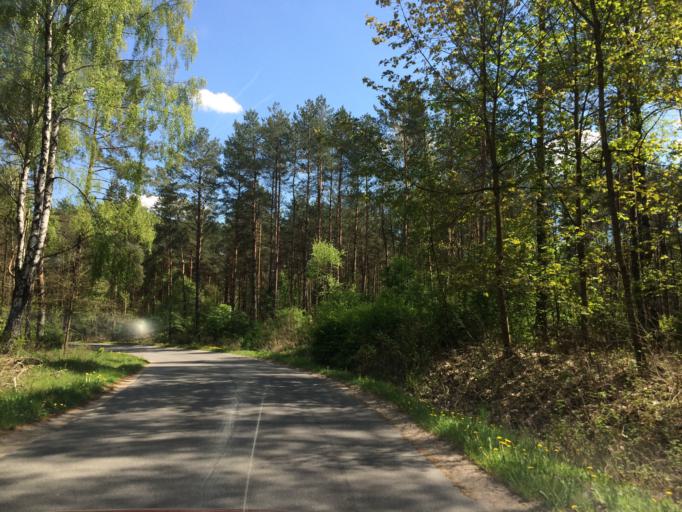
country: PL
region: Warmian-Masurian Voivodeship
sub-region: Powiat ilawski
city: Lubawa
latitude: 53.3886
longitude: 19.7249
